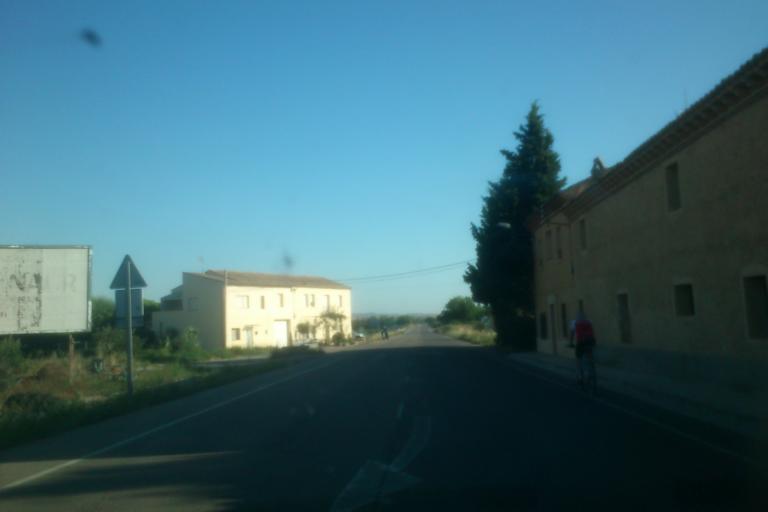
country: ES
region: Aragon
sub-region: Provincia de Zaragoza
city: Villanueva de Gallego
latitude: 41.7628
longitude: -0.7951
